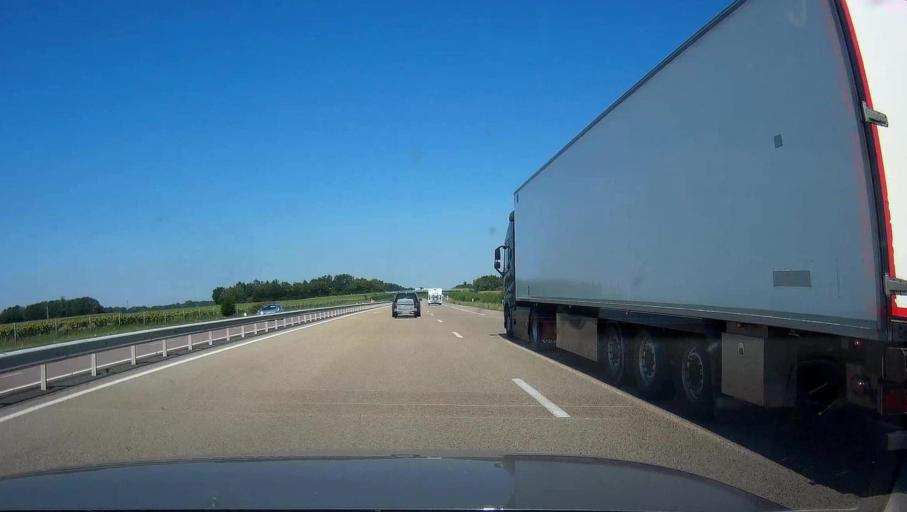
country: FR
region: Champagne-Ardenne
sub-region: Departement de l'Aube
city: Verrieres
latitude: 48.2379
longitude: 4.1732
